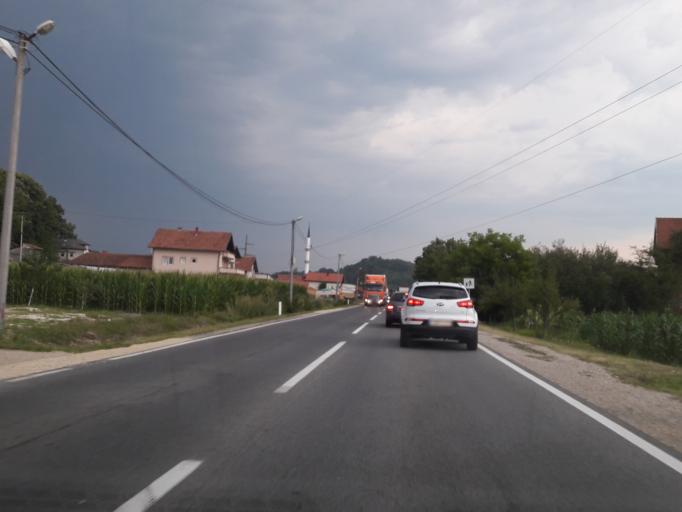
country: BA
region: Federation of Bosnia and Herzegovina
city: Tesanjka
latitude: 44.6545
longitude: 18.0769
